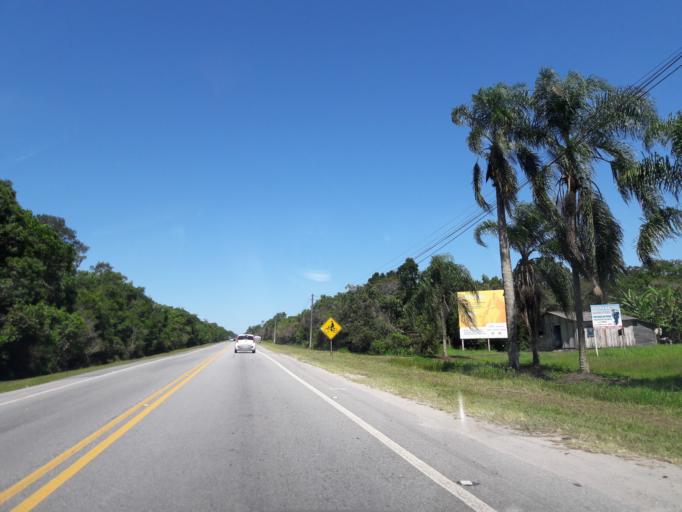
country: BR
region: Parana
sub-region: Pontal Do Parana
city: Pontal do Parana
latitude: -25.6757
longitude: -48.5075
